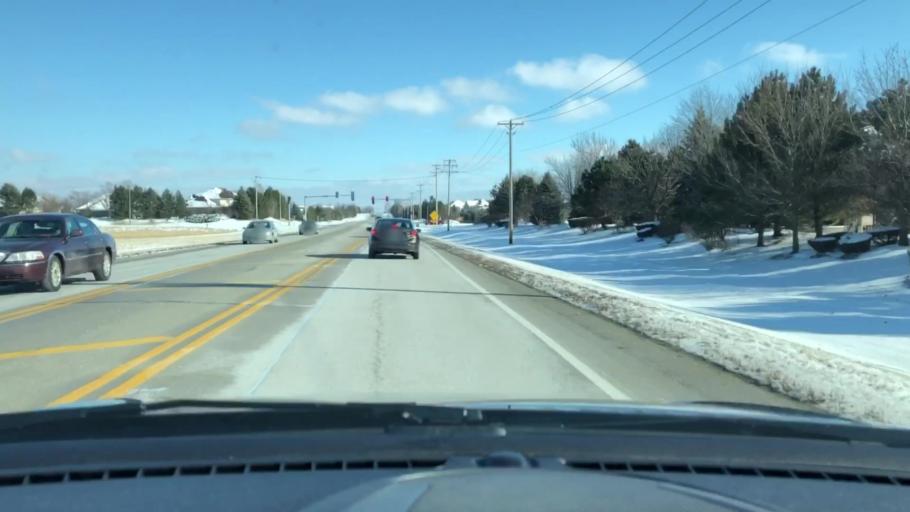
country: US
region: Illinois
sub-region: Will County
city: Mokena
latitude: 41.4838
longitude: -87.8998
